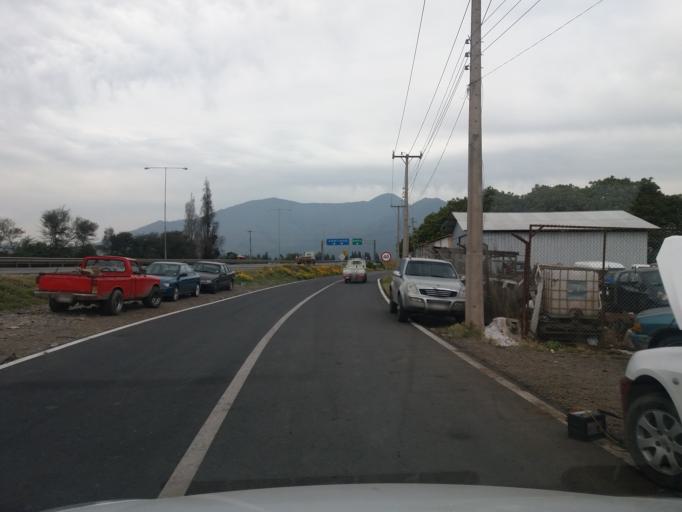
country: CL
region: Valparaiso
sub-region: Provincia de Quillota
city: Hacienda La Calera
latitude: -32.8398
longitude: -71.1129
